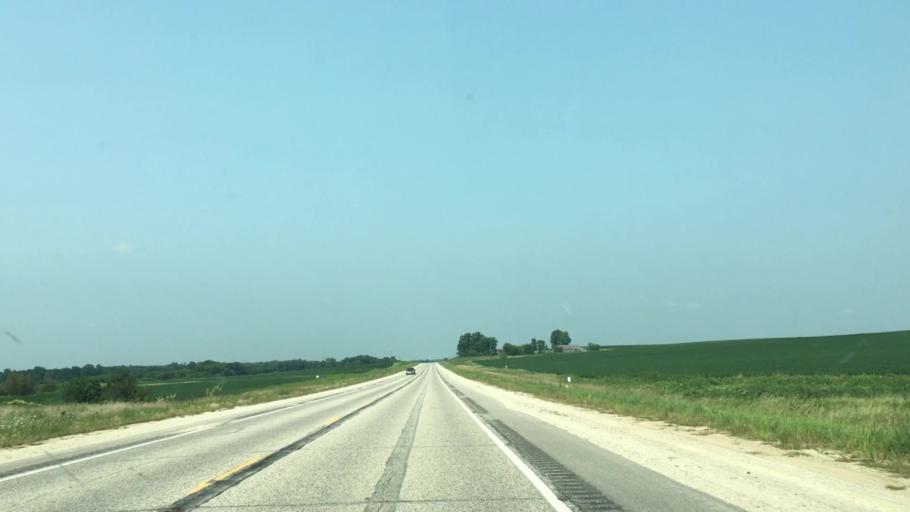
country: US
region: Iowa
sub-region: Fayette County
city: Fayette
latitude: 42.7894
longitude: -91.8048
